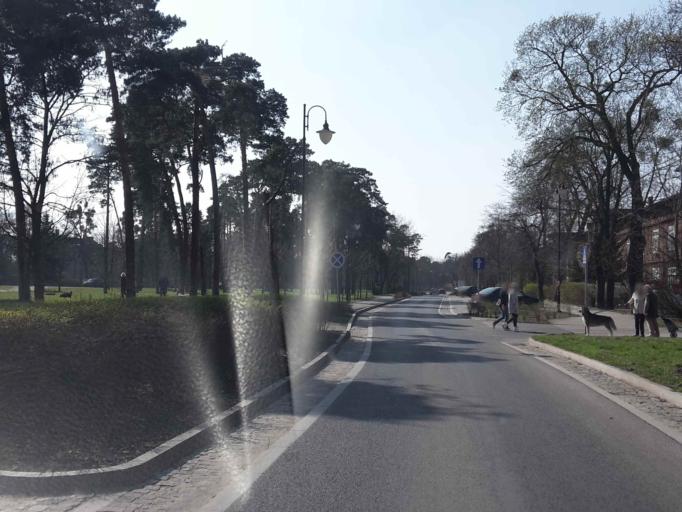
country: PL
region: Kujawsko-Pomorskie
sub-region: Torun
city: Torun
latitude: 53.0118
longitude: 18.5692
